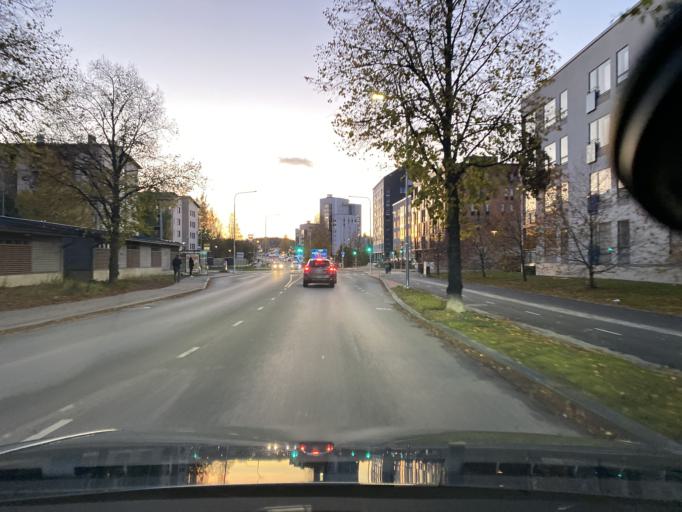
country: FI
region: Pirkanmaa
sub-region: Tampere
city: Tampere
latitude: 61.4708
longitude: 23.7271
